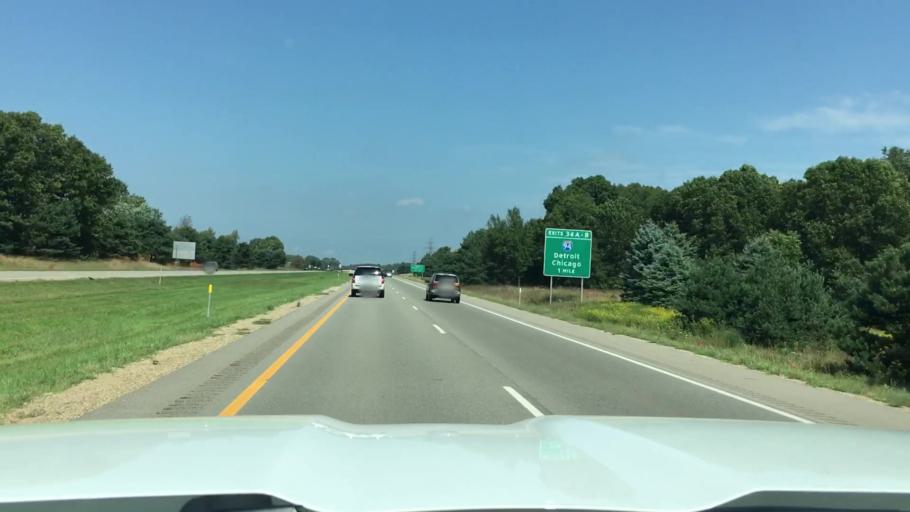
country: US
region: Michigan
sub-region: Kalamazoo County
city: Portage
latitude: 42.2180
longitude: -85.6414
